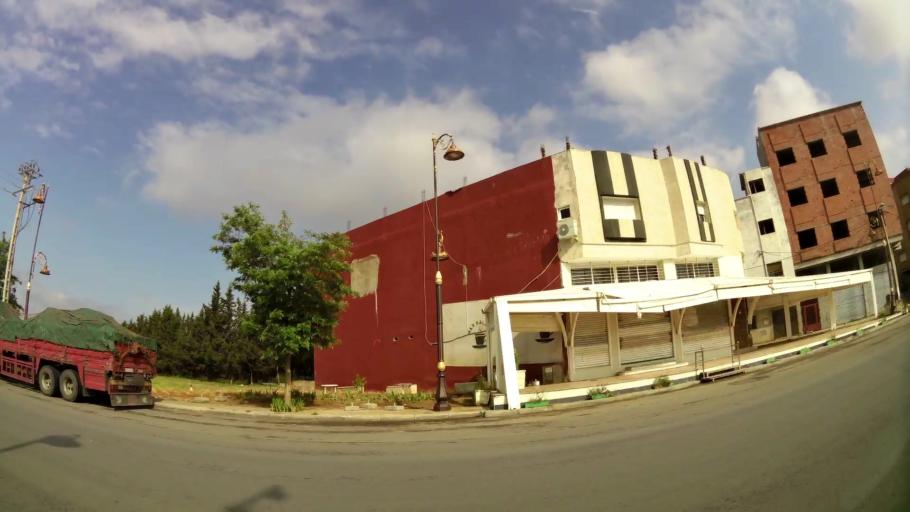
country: MA
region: Rabat-Sale-Zemmour-Zaer
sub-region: Khemisset
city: Tiflet
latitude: 33.8845
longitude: -6.3206
